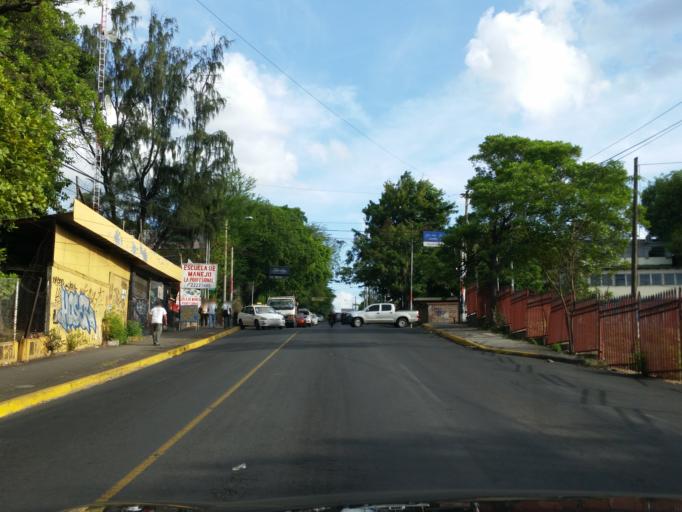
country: NI
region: Managua
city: Managua
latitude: 12.1423
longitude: -86.2752
